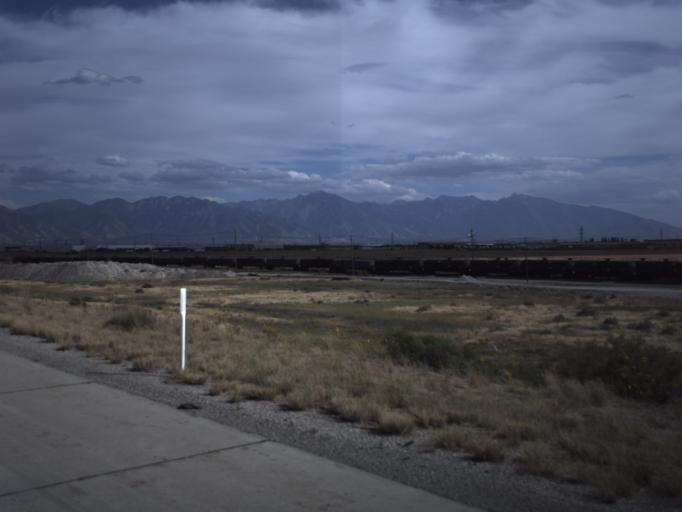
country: US
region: Utah
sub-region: Salt Lake County
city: Magna
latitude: 40.7709
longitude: -112.0436
